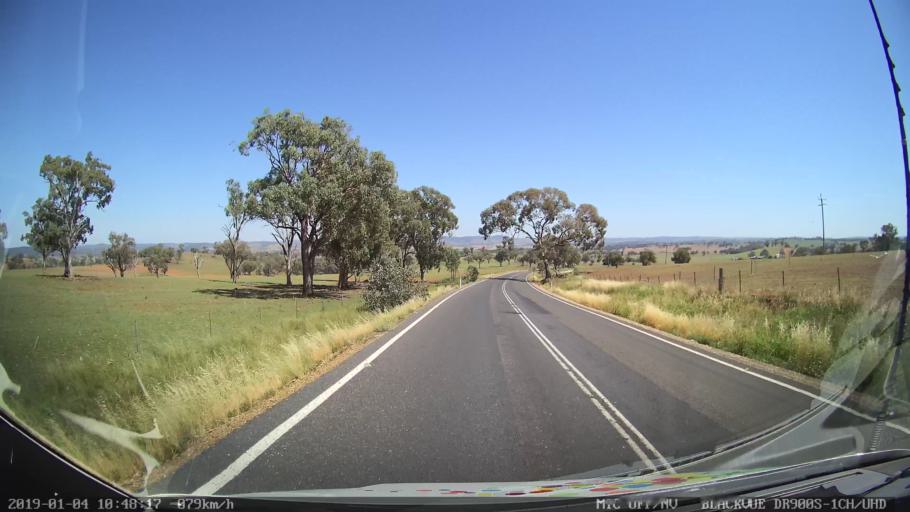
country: AU
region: New South Wales
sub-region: Cabonne
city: Molong
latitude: -33.2618
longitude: 148.7139
